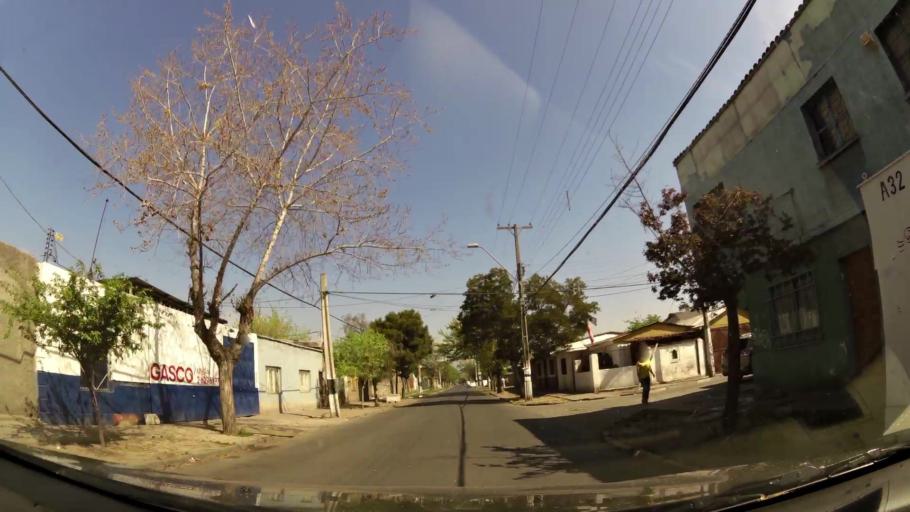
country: CL
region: Santiago Metropolitan
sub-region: Provincia de Santiago
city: Santiago
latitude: -33.3983
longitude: -70.6515
